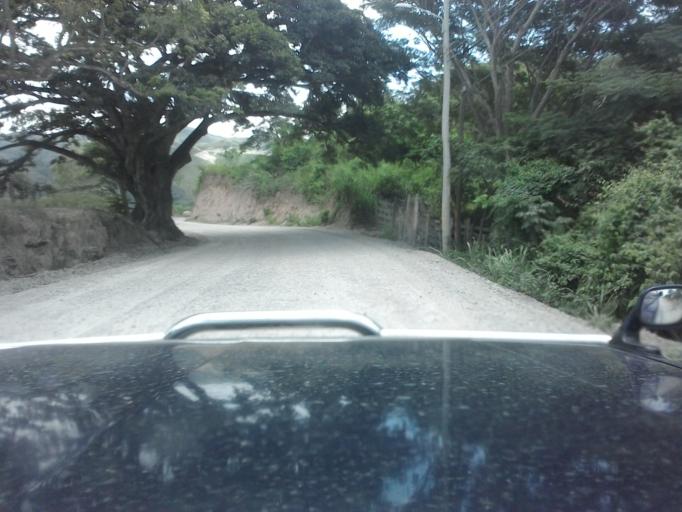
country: CR
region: Guanacaste
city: Juntas
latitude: 10.2425
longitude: -84.8480
